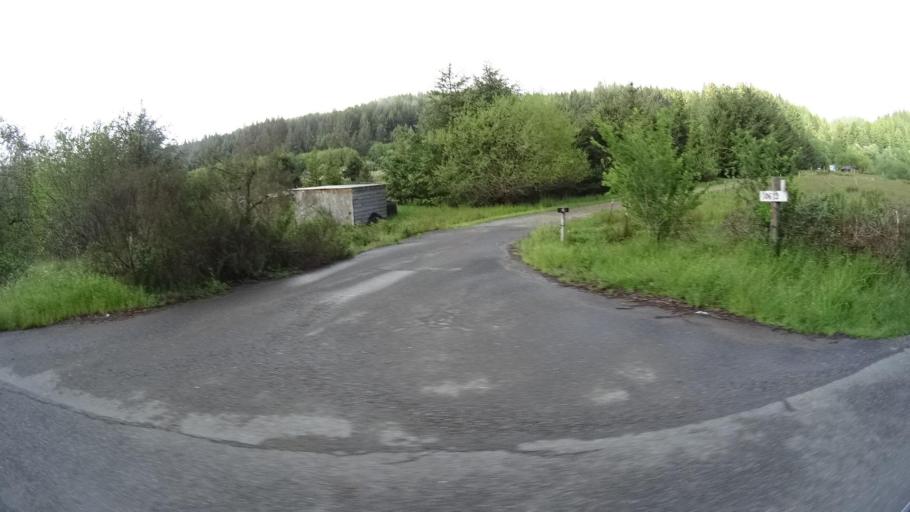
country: US
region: California
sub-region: Humboldt County
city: Blue Lake
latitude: 40.8862
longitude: -124.0331
